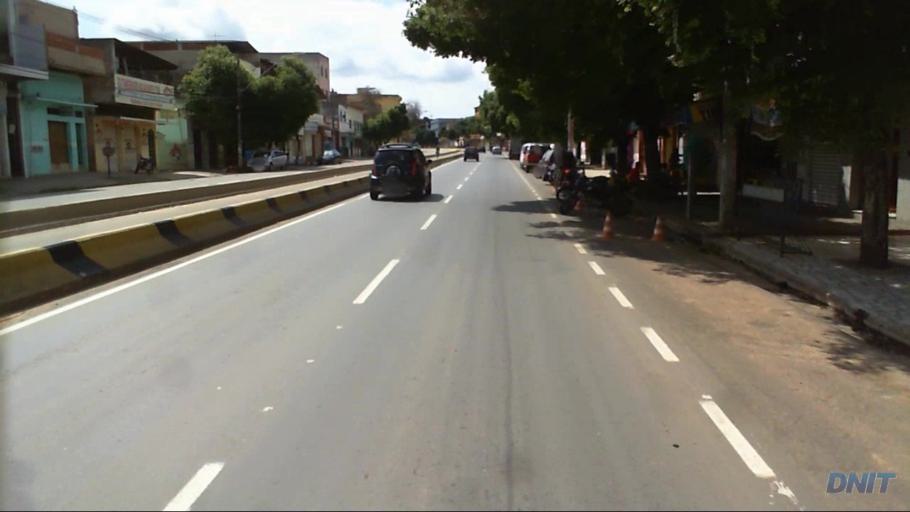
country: BR
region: Minas Gerais
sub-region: Governador Valadares
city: Governador Valadares
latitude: -18.8813
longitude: -41.9643
